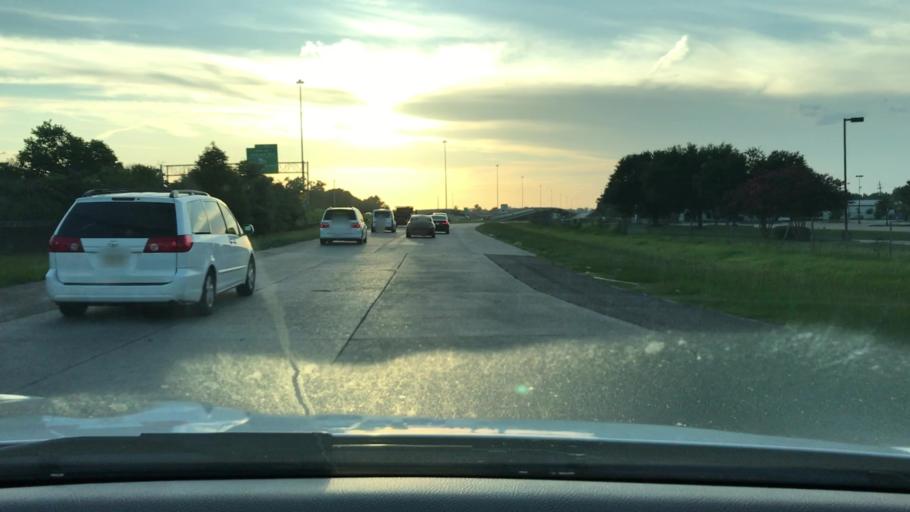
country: US
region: Louisiana
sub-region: East Baton Rouge Parish
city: Village Saint George
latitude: 30.3833
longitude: -91.0661
